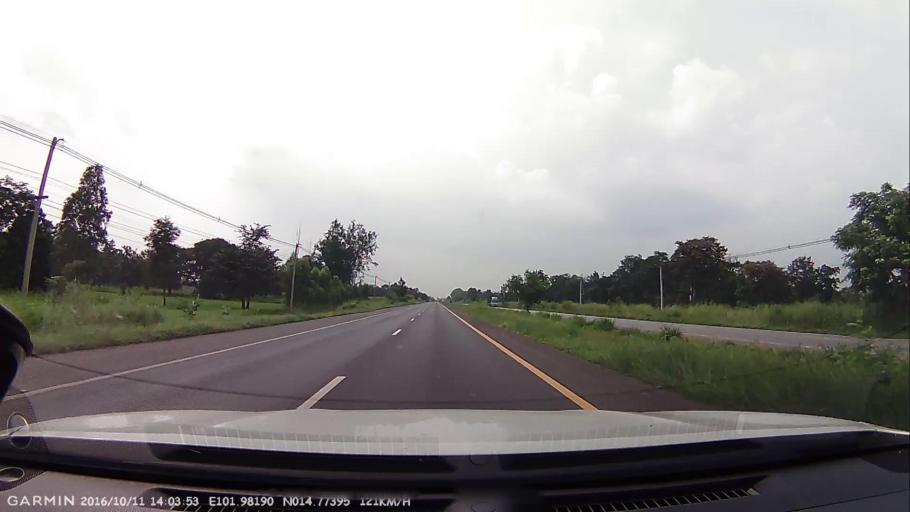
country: TH
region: Nakhon Ratchasima
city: Pak Thong Chai
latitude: 14.7740
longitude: 101.9817
